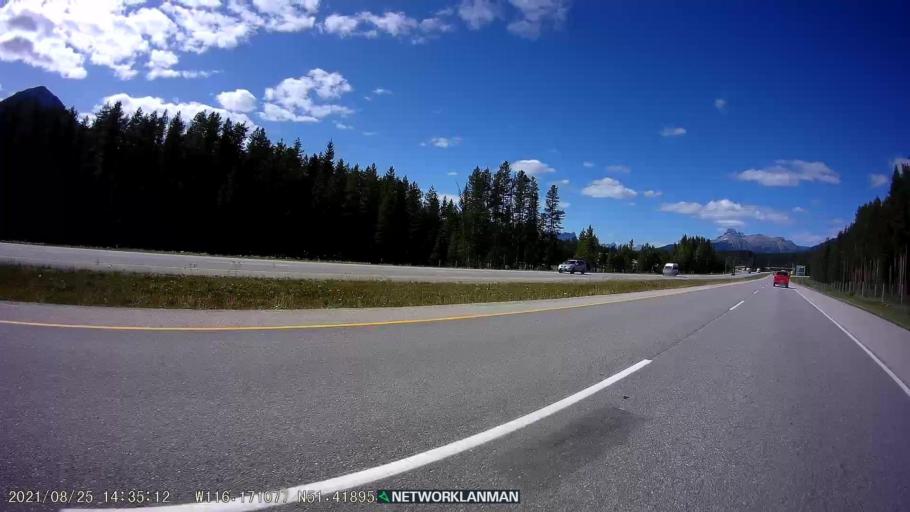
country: CA
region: Alberta
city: Lake Louise
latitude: 51.4189
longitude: -116.1709
